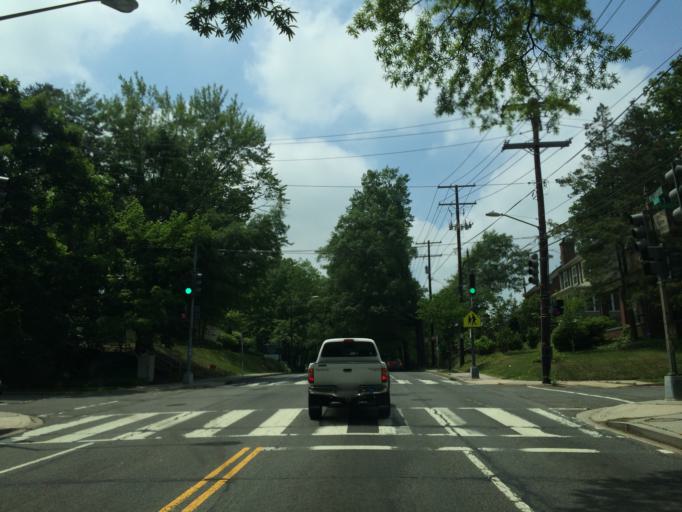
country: US
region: Maryland
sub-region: Montgomery County
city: Chevy Chase
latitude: 38.9610
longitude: -77.0619
